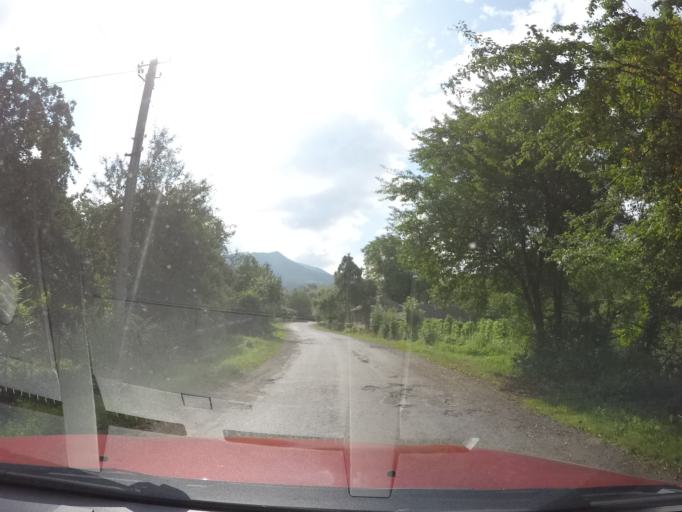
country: UA
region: Zakarpattia
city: Velykyi Bereznyi
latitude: 48.9458
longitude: 22.6186
